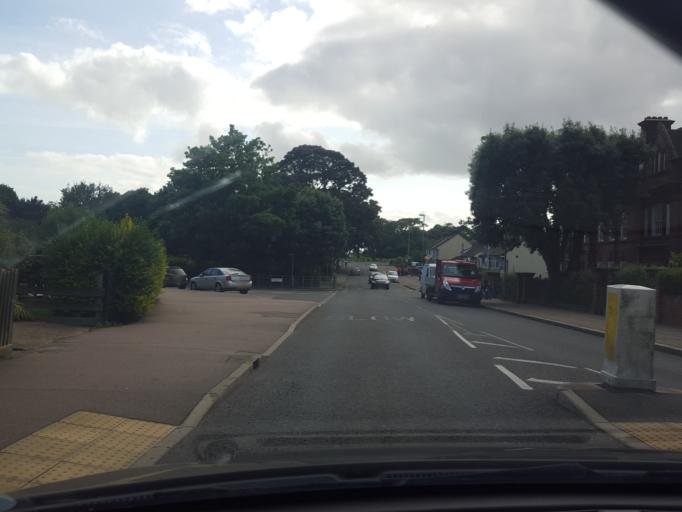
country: GB
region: England
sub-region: Essex
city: Harwich
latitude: 51.9406
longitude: 1.2865
